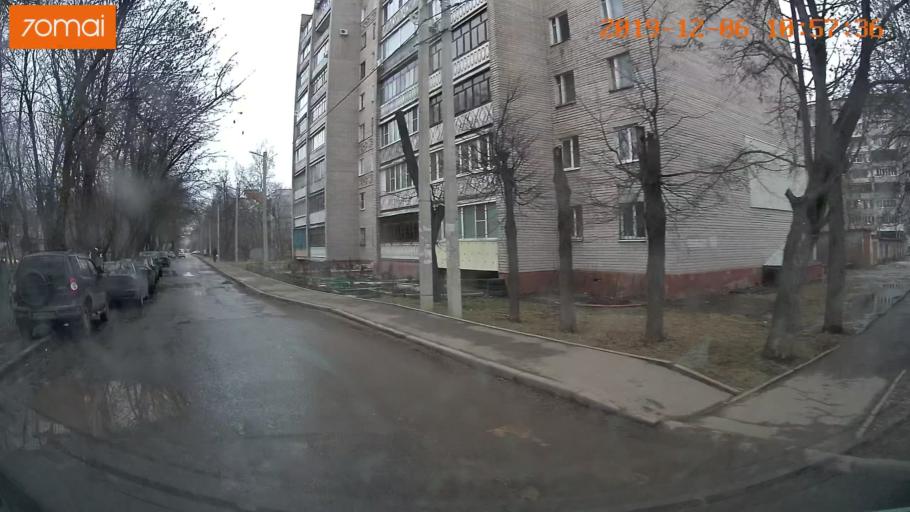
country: RU
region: Ivanovo
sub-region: Gorod Ivanovo
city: Ivanovo
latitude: 56.9673
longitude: 40.9777
